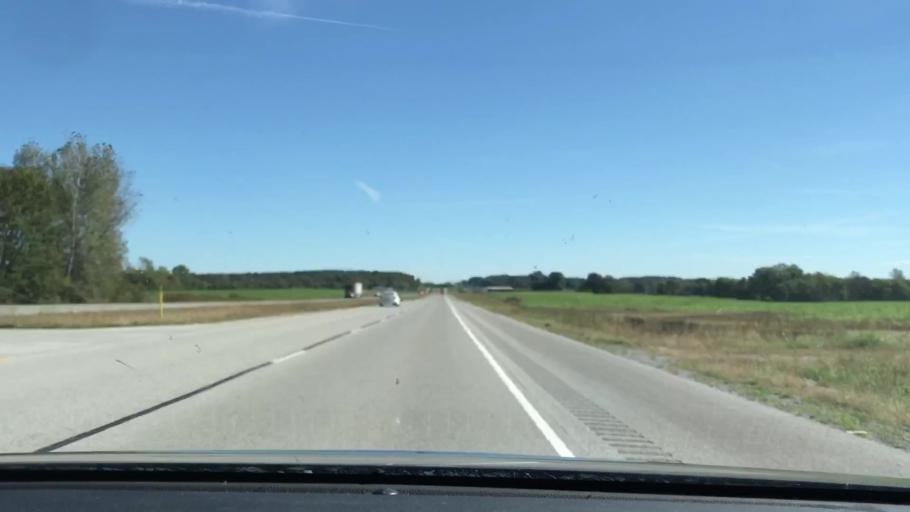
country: US
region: Kentucky
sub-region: Logan County
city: Auburn
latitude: 36.8542
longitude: -86.7625
